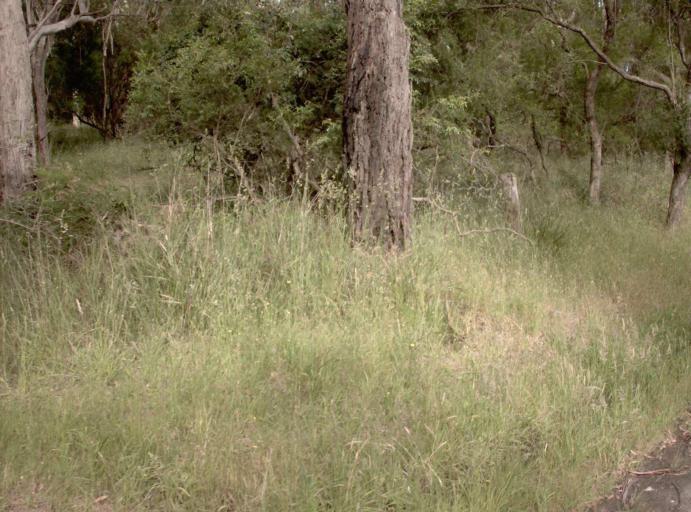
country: AU
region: Victoria
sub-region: Bass Coast
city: Phillip Island
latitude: -38.4854
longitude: 145.2609
